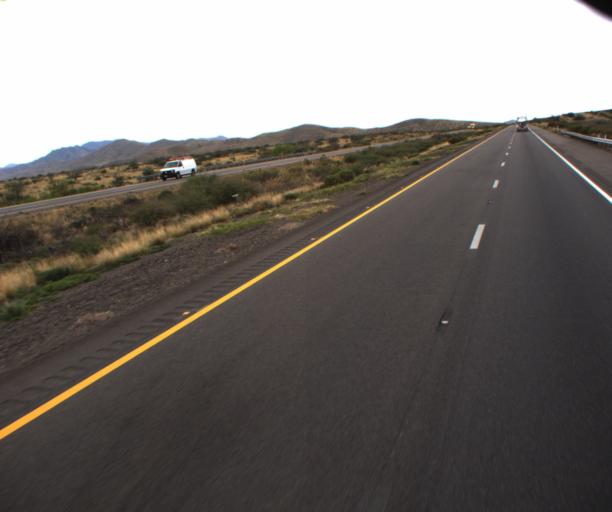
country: US
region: Arizona
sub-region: Cochise County
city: Willcox
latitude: 32.1320
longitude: -110.0080
